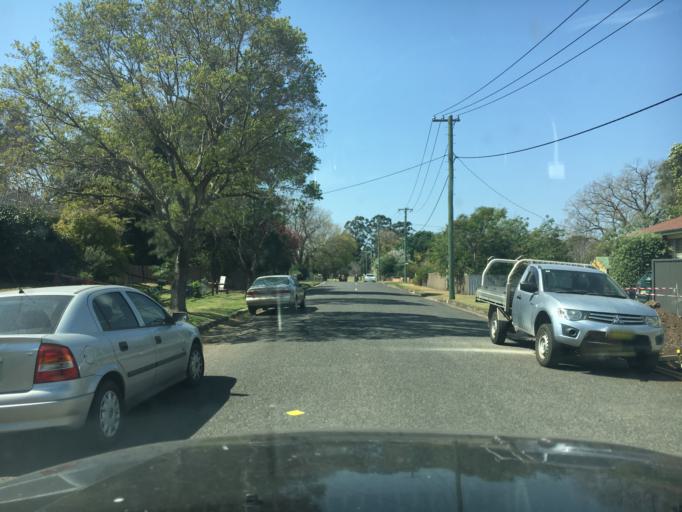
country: AU
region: New South Wales
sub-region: Singleton
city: Singleton
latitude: -32.5634
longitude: 151.1789
